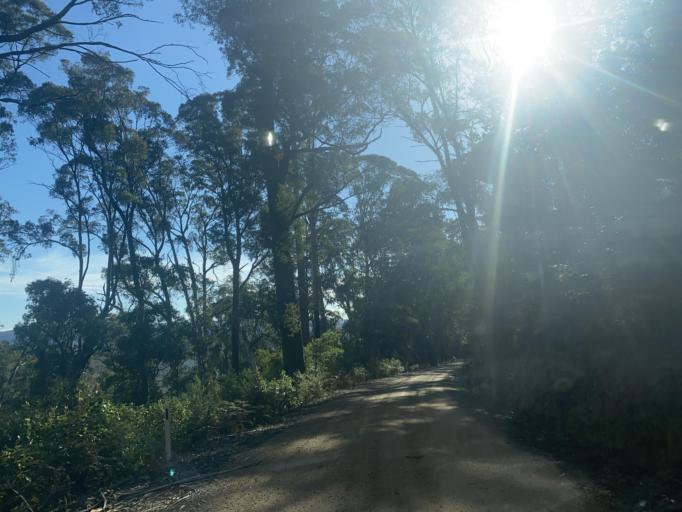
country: AU
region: Victoria
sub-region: Mansfield
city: Mansfield
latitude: -36.8449
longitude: 146.1703
